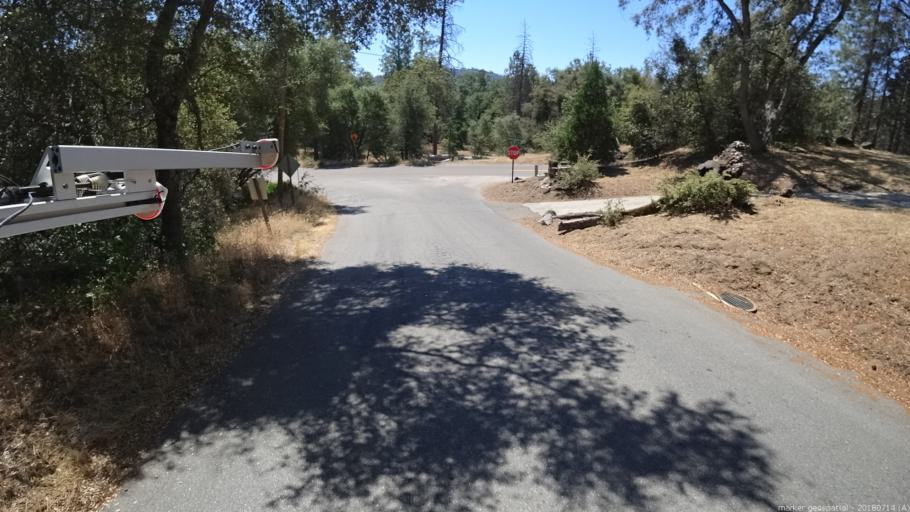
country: US
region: California
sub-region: Madera County
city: Oakhurst
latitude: 37.3721
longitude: -119.6325
